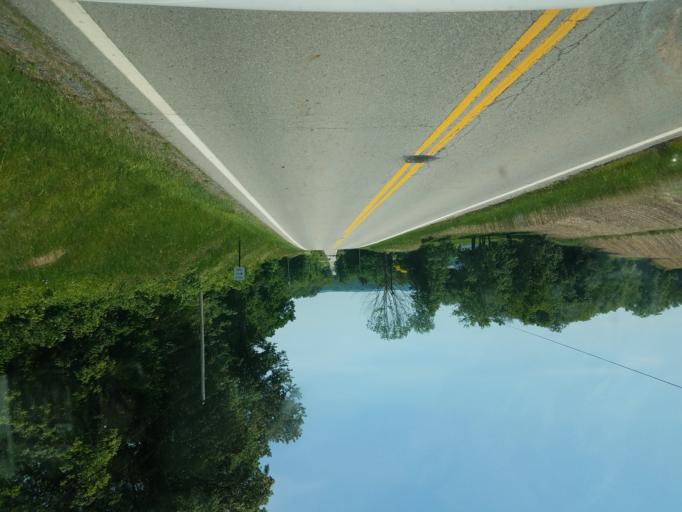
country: US
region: Ohio
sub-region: Ashland County
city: Loudonville
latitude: 40.6925
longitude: -82.2643
